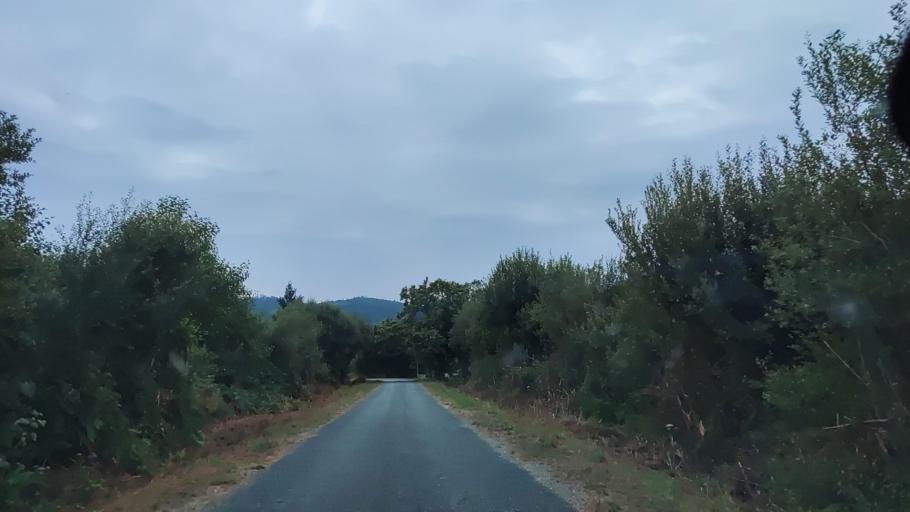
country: ES
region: Galicia
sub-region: Provincia de Pontevedra
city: Catoira
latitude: 42.7151
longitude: -8.7144
